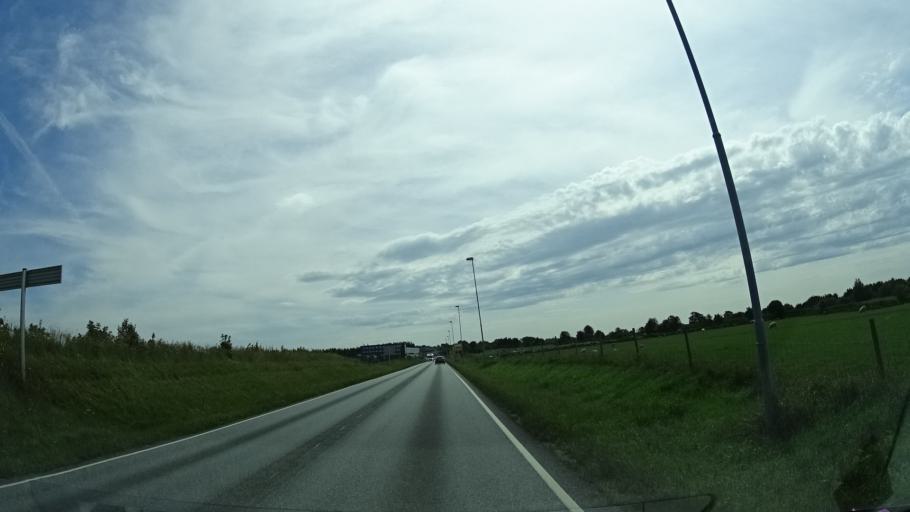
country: NO
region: Rogaland
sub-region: Randaberg
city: Randaberg
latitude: 58.9986
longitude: 5.6471
